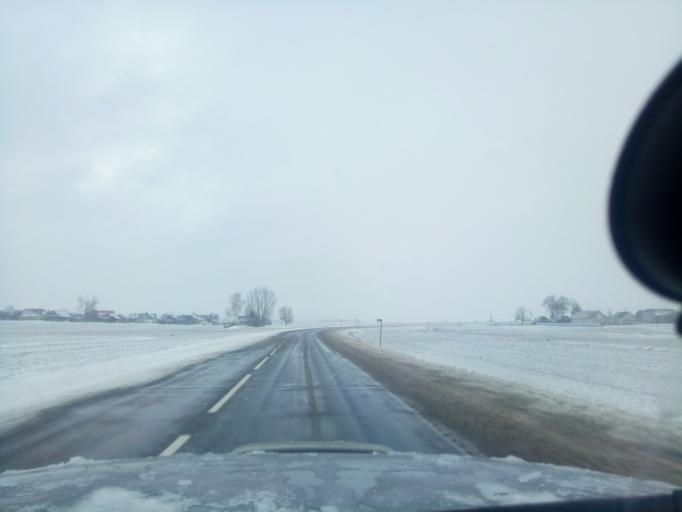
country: BY
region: Minsk
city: Haradzyeya
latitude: 53.3030
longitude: 26.5741
